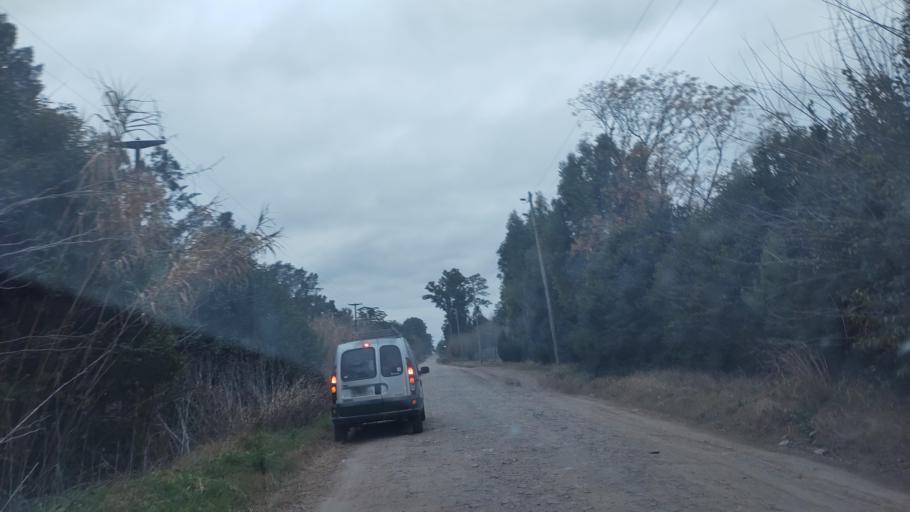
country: AR
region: Buenos Aires
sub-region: Partido de La Plata
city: La Plata
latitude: -34.8644
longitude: -58.1196
